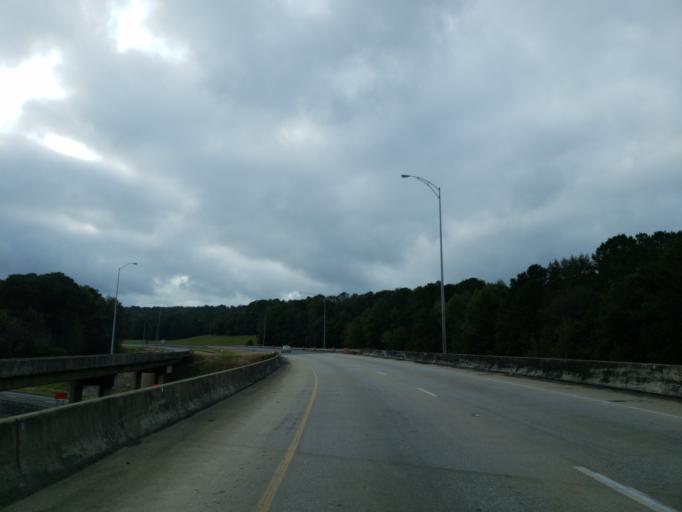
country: US
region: Alabama
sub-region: Jefferson County
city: Bessemer
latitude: 33.3429
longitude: -87.0269
